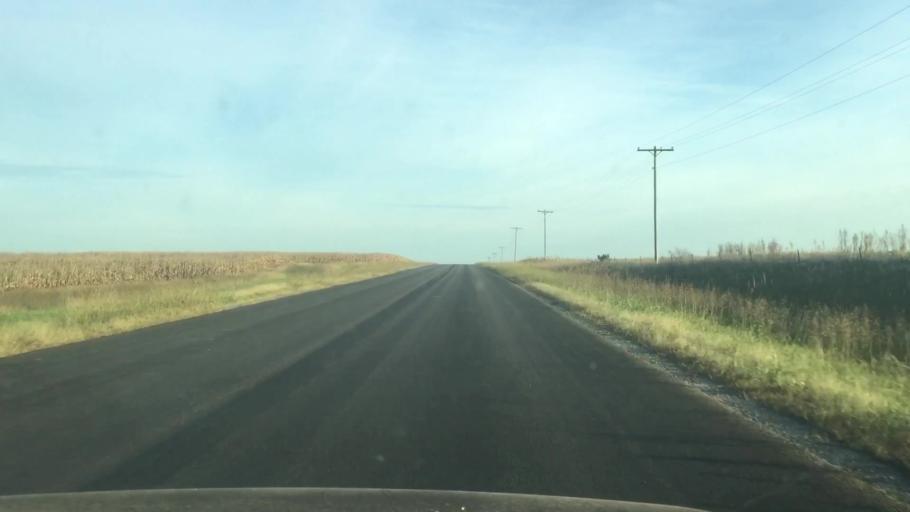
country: US
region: Kansas
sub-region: Marshall County
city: Marysville
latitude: 39.9173
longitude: -96.6009
